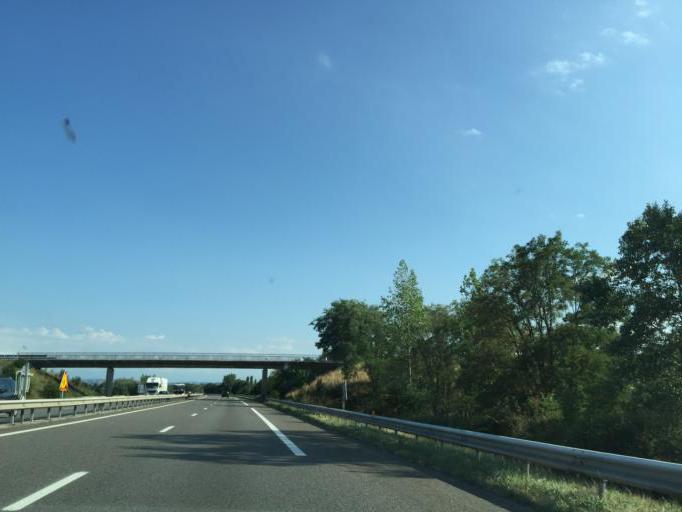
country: FR
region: Rhone-Alpes
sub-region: Departement de la Loire
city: Cuzieu
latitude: 45.5825
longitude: 4.2137
